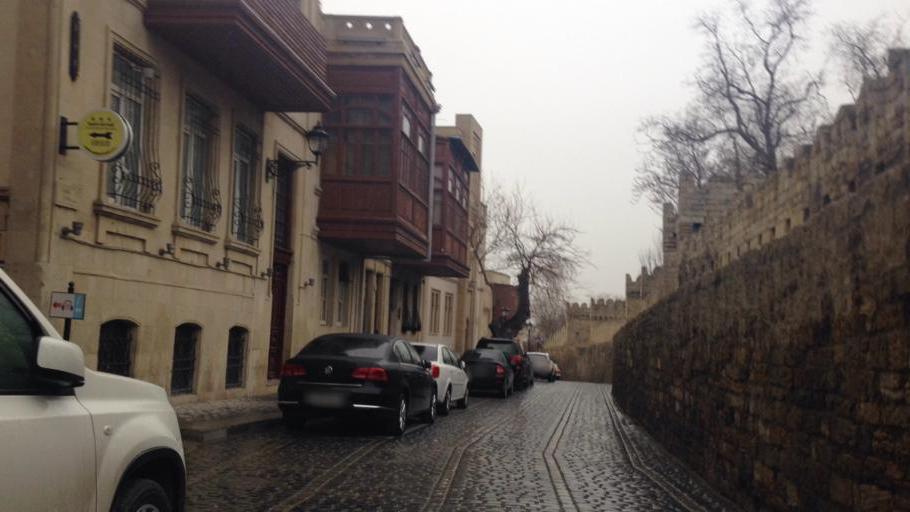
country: AZ
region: Baki
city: Badamdar
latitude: 40.3655
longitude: 49.8322
